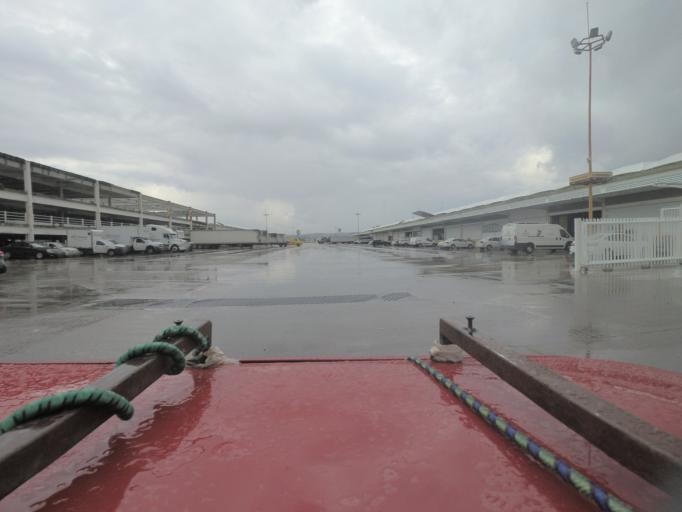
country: MX
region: Aguascalientes
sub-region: Jesus Maria
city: Arboledas Paso Blanco [Fraccionamiento]
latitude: 21.9716
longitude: -102.2927
